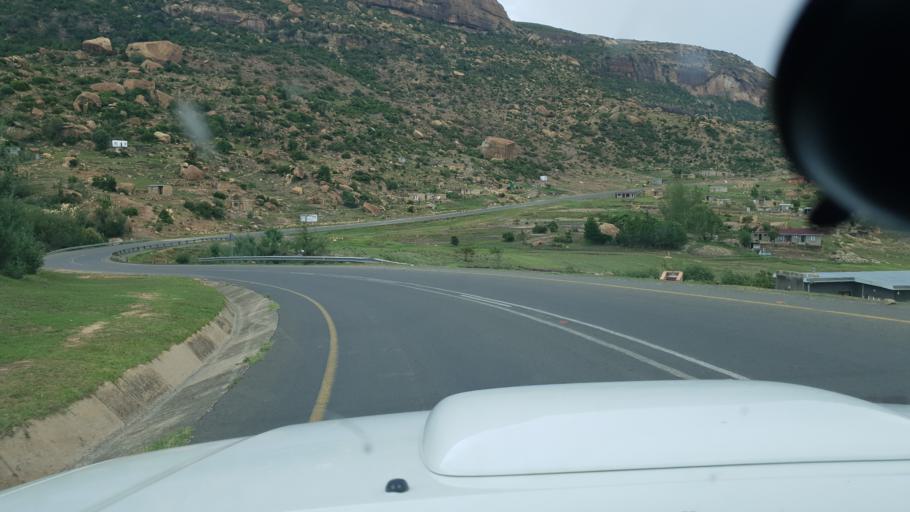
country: LS
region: Maseru
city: Maseru
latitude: -29.4651
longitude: 27.4971
